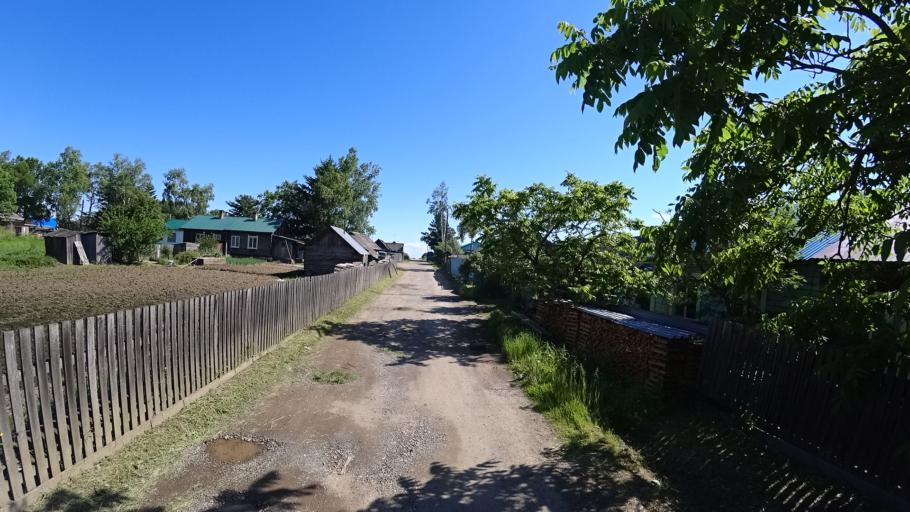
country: RU
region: Khabarovsk Krai
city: Khor
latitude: 47.8888
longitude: 135.0266
